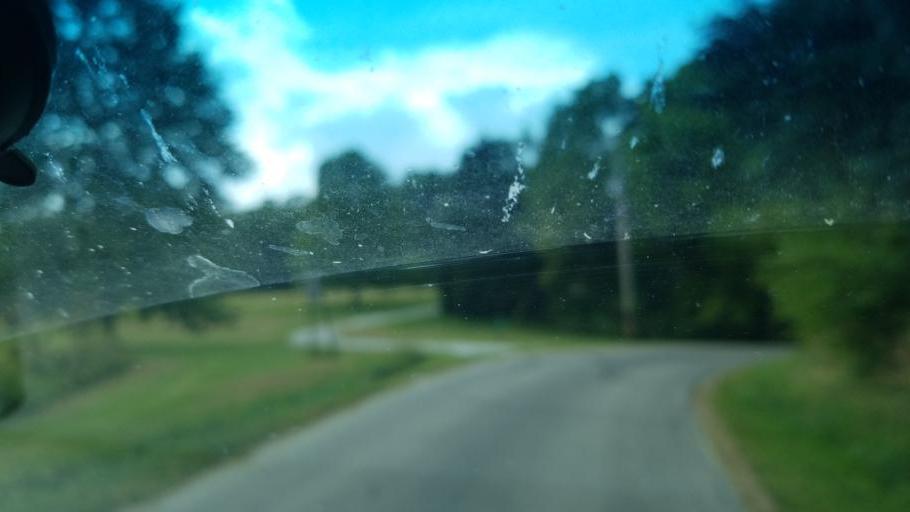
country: US
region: Ohio
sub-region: Seneca County
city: Tiffin
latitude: 40.9554
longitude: -83.1508
